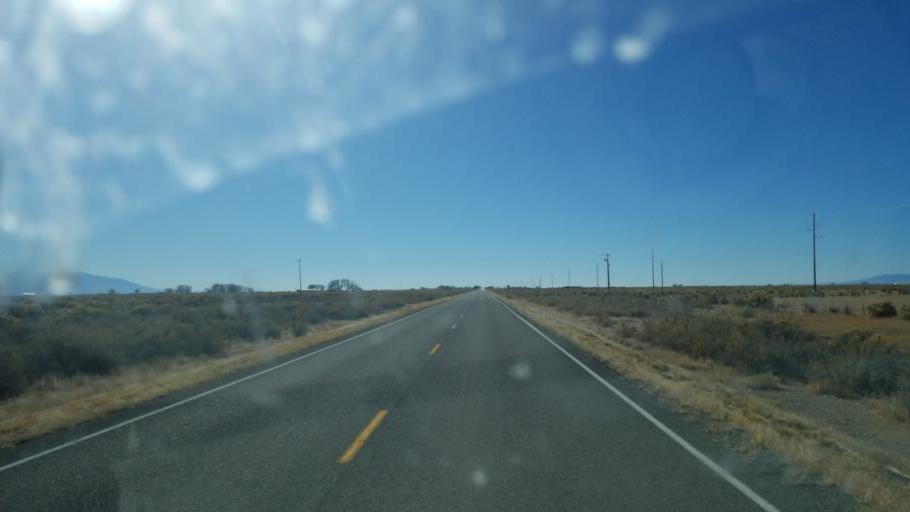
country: US
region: Colorado
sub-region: Saguache County
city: Saguache
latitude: 38.0507
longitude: -105.9142
